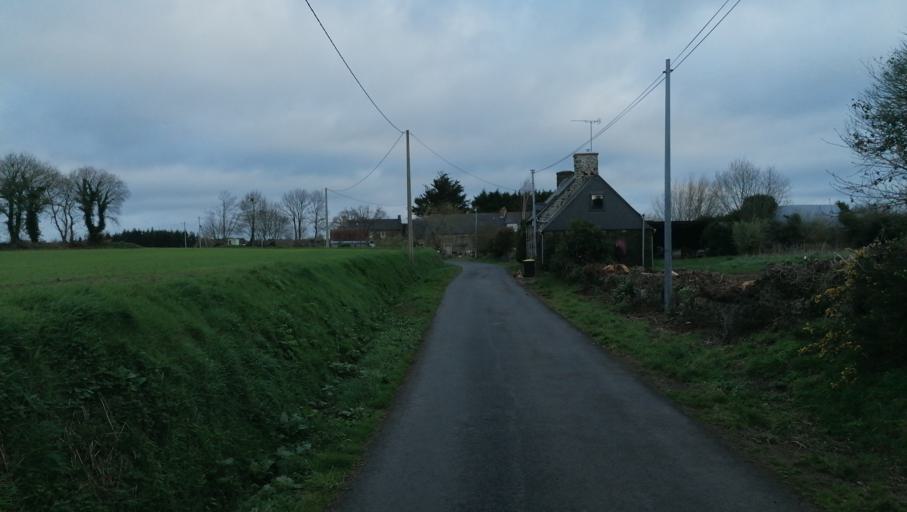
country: FR
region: Brittany
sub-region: Departement des Cotes-d'Armor
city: Pommerit-le-Vicomte
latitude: 48.6462
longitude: -3.0682
